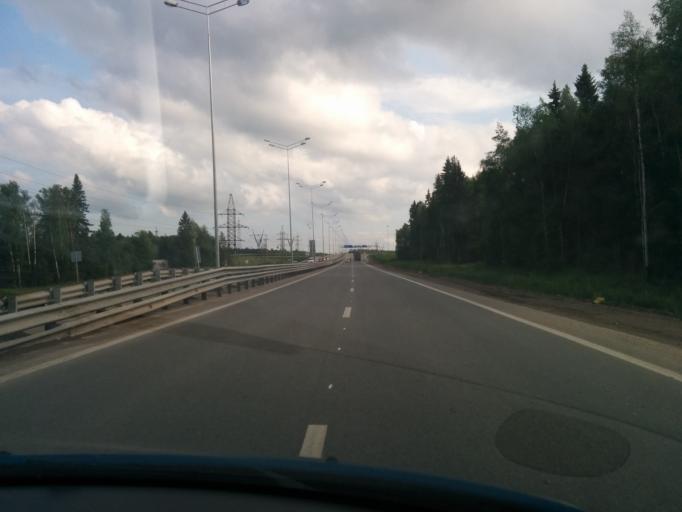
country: RU
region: Perm
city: Novyye Lyady
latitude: 58.0531
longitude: 56.4285
